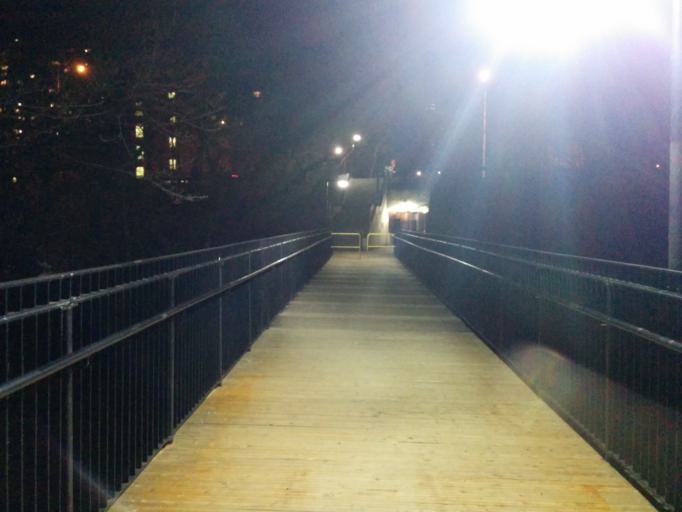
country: CA
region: Ontario
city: Toronto
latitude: 43.6729
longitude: -79.3749
